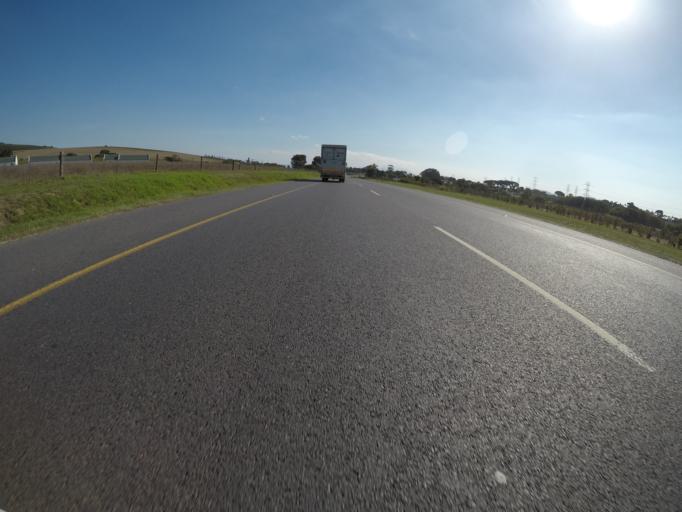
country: ZA
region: Western Cape
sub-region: City of Cape Town
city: Kraaifontein
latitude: -33.9012
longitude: 18.7254
